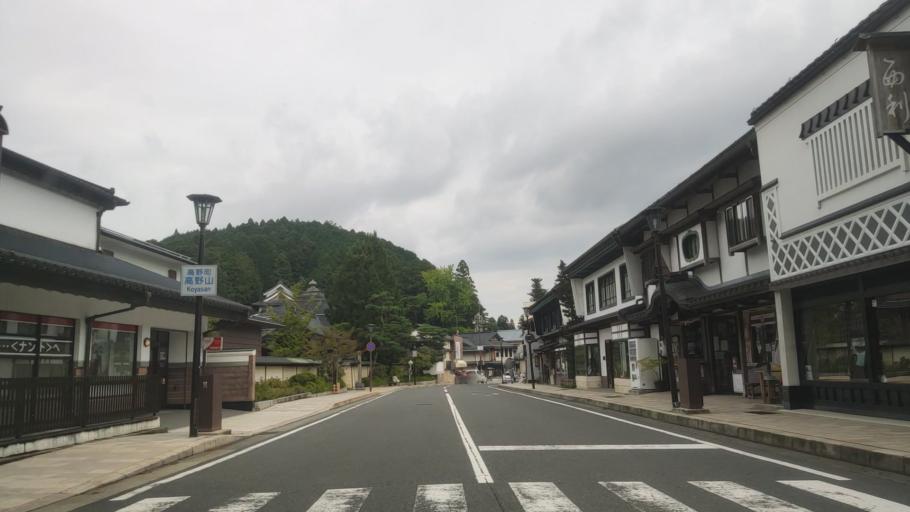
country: JP
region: Wakayama
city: Koya
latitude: 34.2132
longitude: 135.5850
